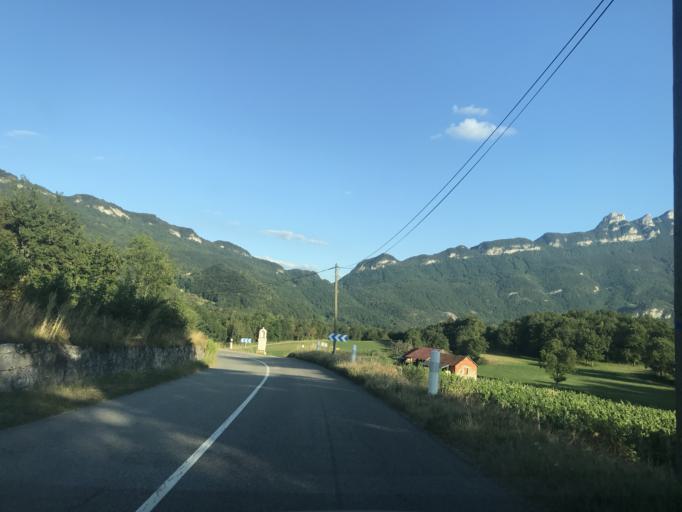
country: FR
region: Rhone-Alpes
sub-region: Departement de la Savoie
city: Yenne
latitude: 45.7162
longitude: 5.8129
